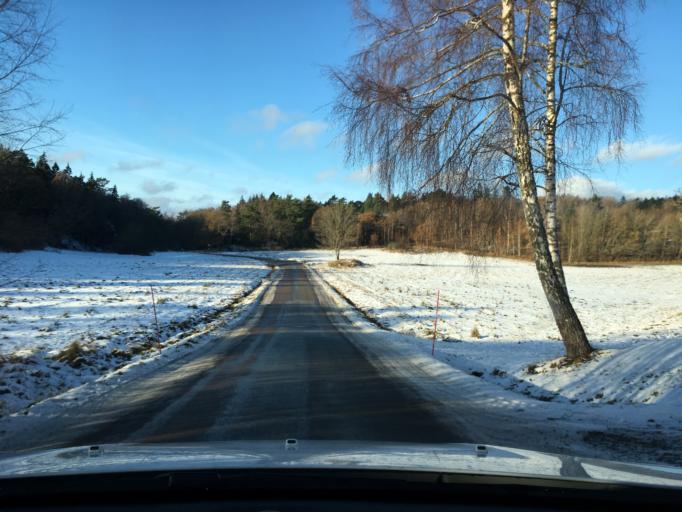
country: SE
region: Vaestra Goetaland
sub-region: Tjorns Kommun
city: Myggenas
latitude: 58.0971
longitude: 11.7154
